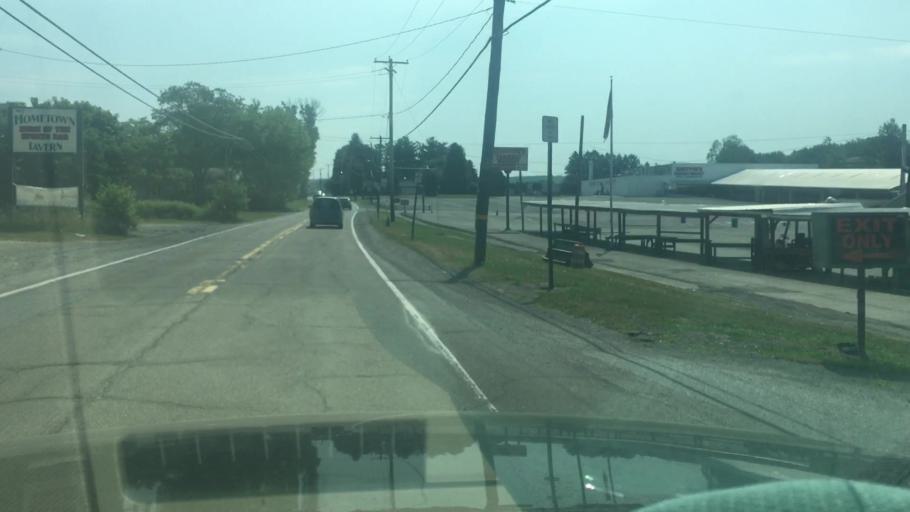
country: US
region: Pennsylvania
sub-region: Schuylkill County
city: Hometown
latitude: 40.8221
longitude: -75.9932
